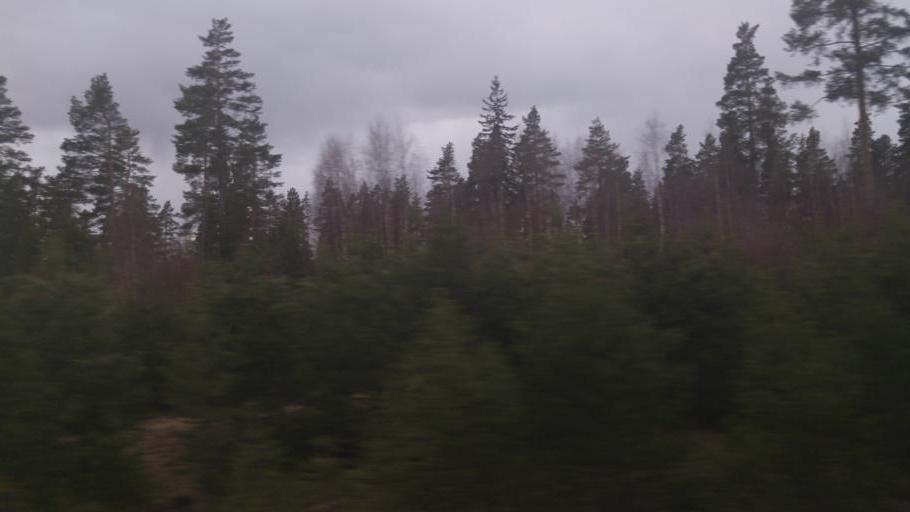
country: NO
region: Akershus
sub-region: Eidsvoll
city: Raholt
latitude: 60.2325
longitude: 11.1106
